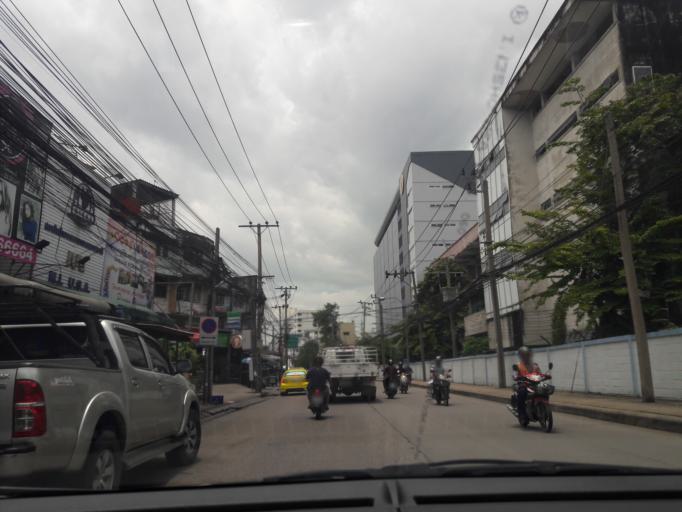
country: TH
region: Bangkok
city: Bang Kapi
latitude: 13.7529
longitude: 100.6192
